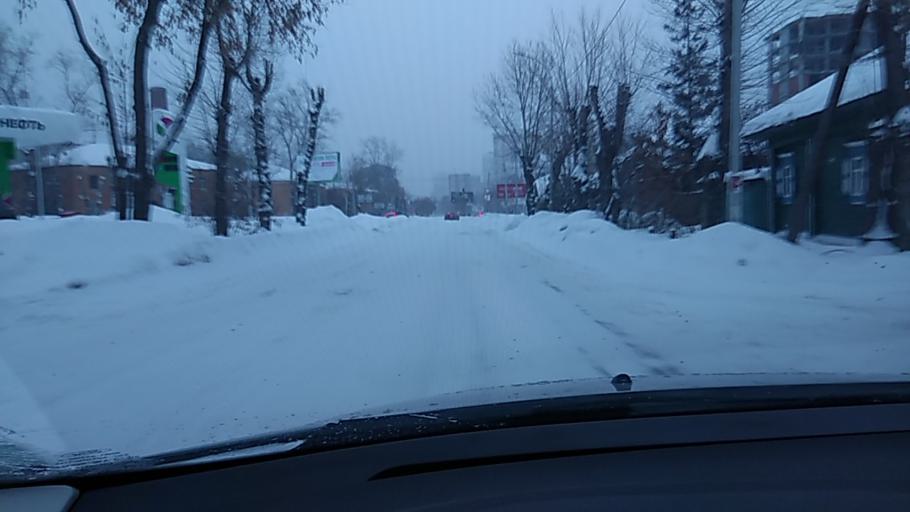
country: RU
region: Sverdlovsk
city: Sovkhoznyy
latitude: 56.8218
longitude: 60.5513
